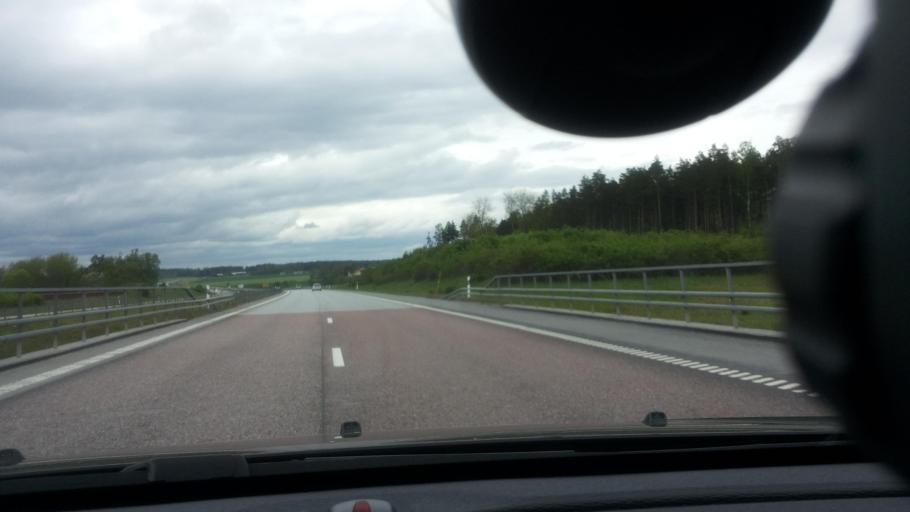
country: SE
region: Uppsala
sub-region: Uppsala Kommun
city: Storvreta
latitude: 59.9401
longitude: 17.6604
